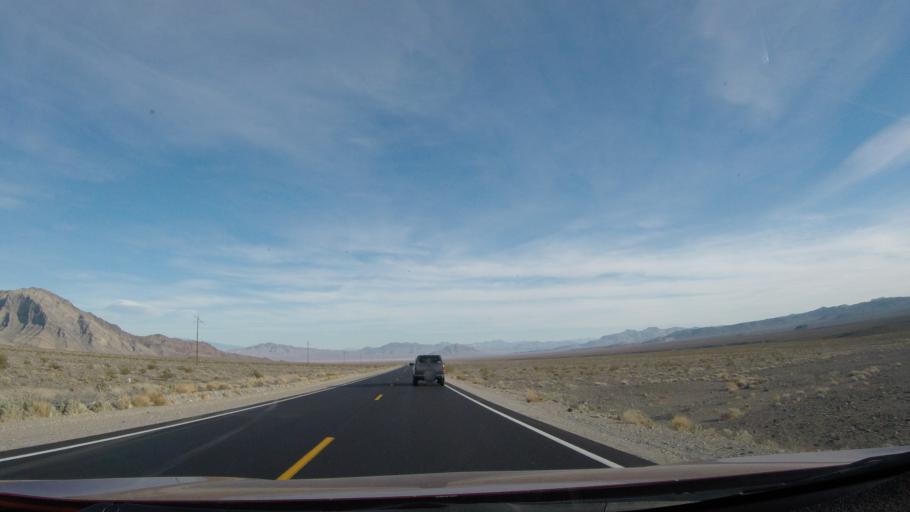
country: US
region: Nevada
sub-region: Nye County
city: Pahrump
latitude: 36.3275
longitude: -116.5688
